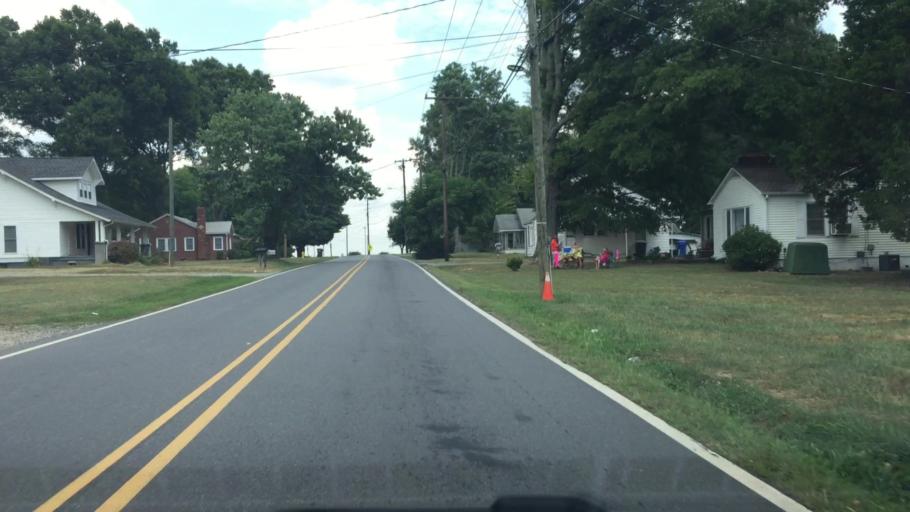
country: US
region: North Carolina
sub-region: Iredell County
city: Troutman
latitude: 35.7111
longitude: -80.8933
